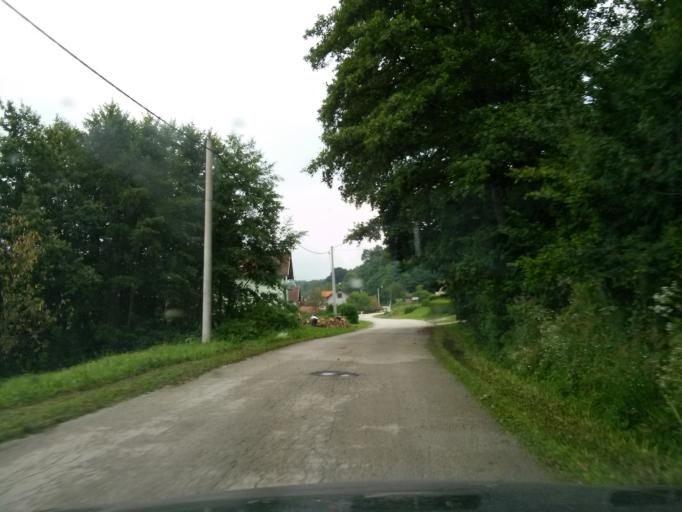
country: HR
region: Sisacko-Moslavacka
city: Glina
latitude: 45.3061
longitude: 15.9857
